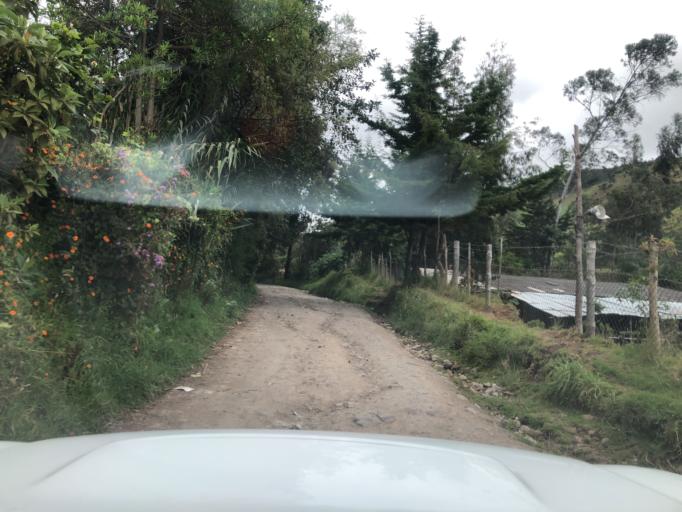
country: CO
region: Cauca
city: Totoro
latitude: 2.5120
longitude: -76.3737
